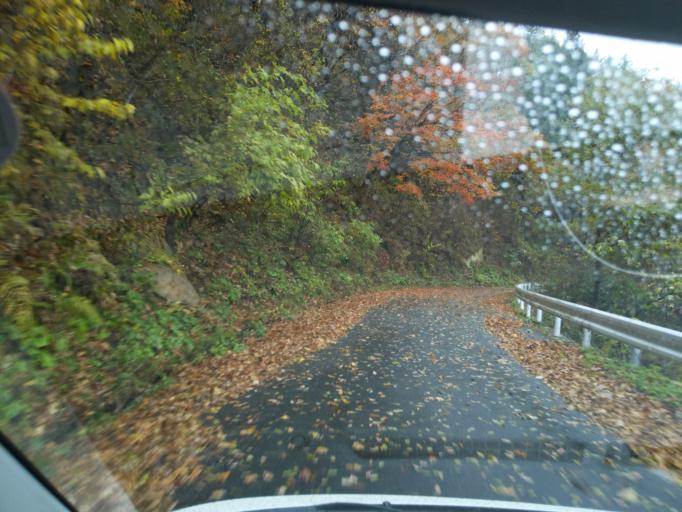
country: JP
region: Iwate
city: Mizusawa
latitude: 39.1022
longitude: 140.9403
